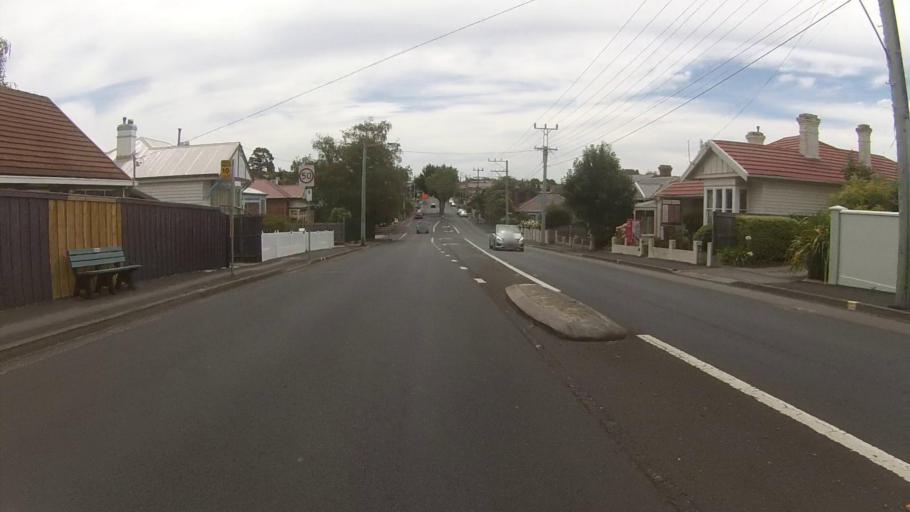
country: AU
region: Tasmania
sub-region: Hobart
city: Sandy Bay
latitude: -42.8989
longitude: 147.3243
